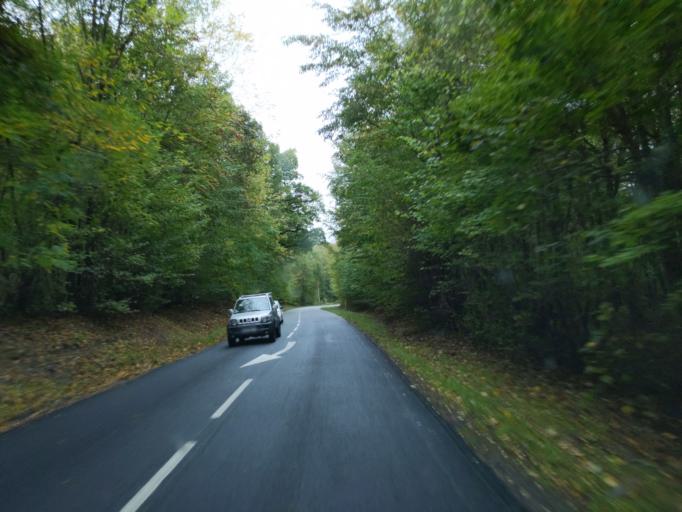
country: FR
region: Ile-de-France
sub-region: Departement des Yvelines
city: Bullion
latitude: 48.6057
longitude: 1.9963
